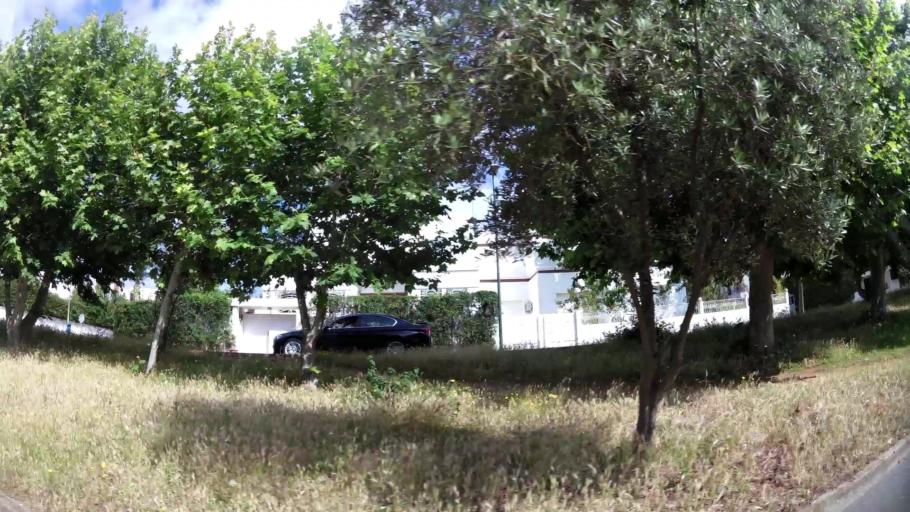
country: MA
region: Rabat-Sale-Zemmour-Zaer
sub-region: Skhirate-Temara
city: Temara
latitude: 33.9495
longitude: -6.8705
